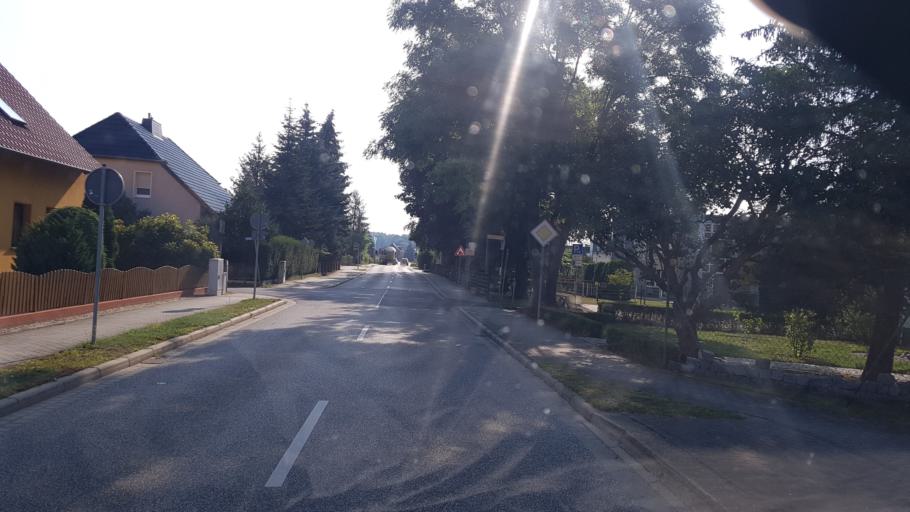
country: DE
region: Brandenburg
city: Drebkau
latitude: 51.6951
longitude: 14.2538
